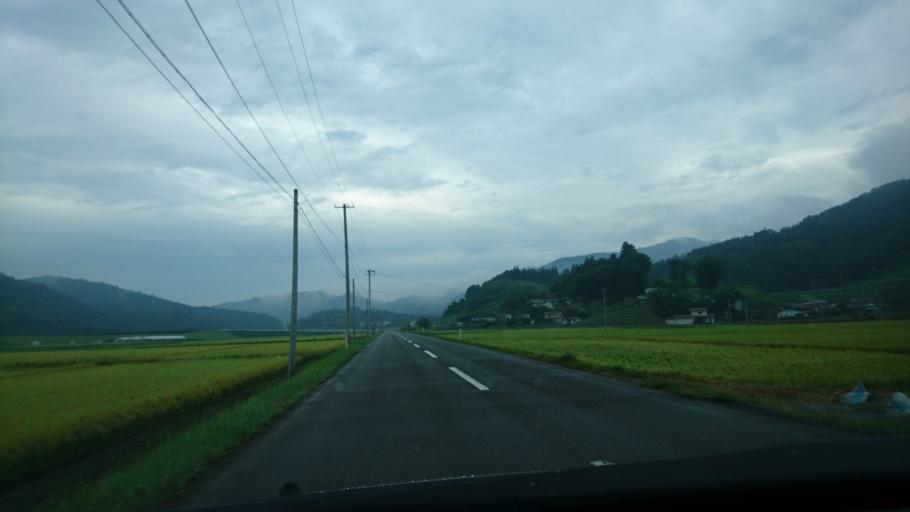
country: JP
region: Iwate
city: Ichinoseki
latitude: 38.9412
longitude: 141.2500
